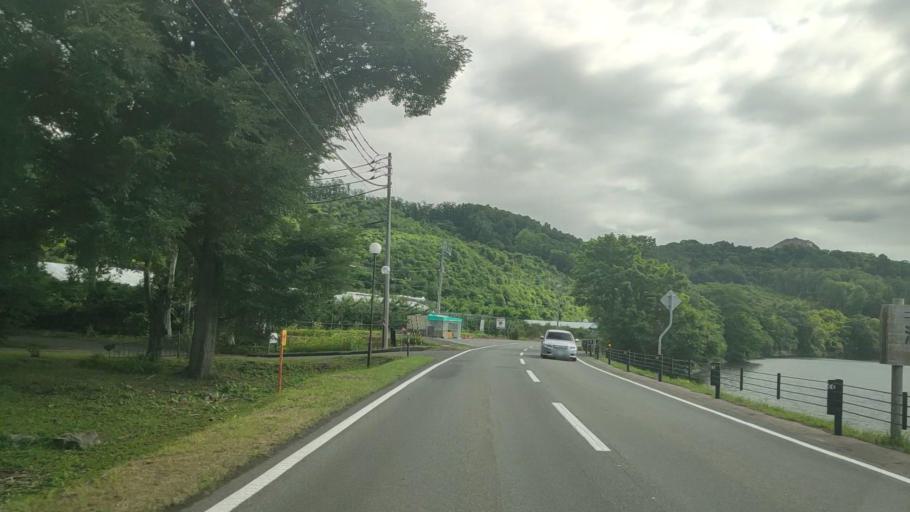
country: JP
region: Hokkaido
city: Date
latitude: 42.5610
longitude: 140.8778
